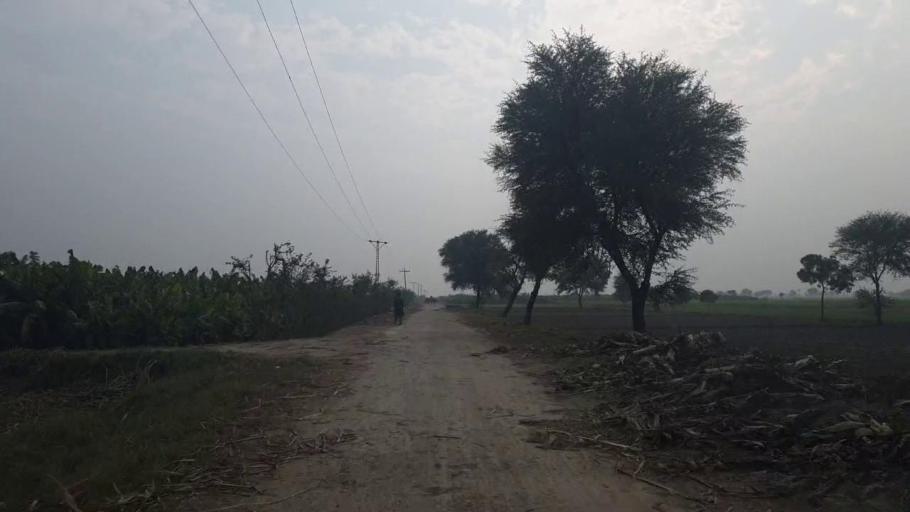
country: PK
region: Sindh
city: Berani
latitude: 25.7967
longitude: 68.7313
